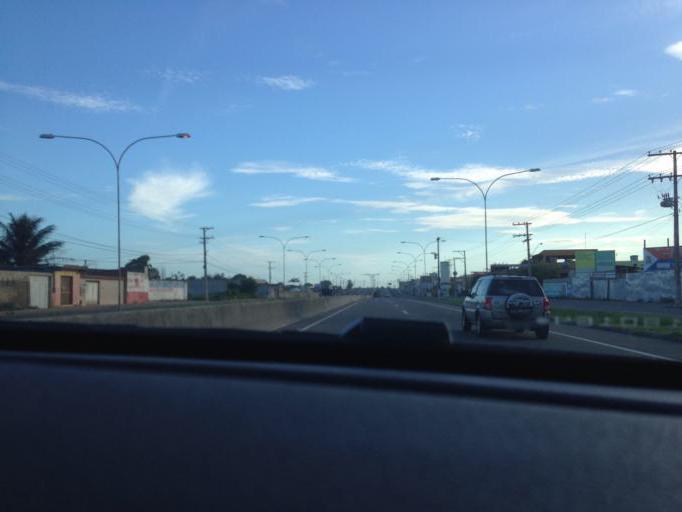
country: BR
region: Espirito Santo
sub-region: Vila Velha
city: Vila Velha
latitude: -20.4436
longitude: -40.3332
